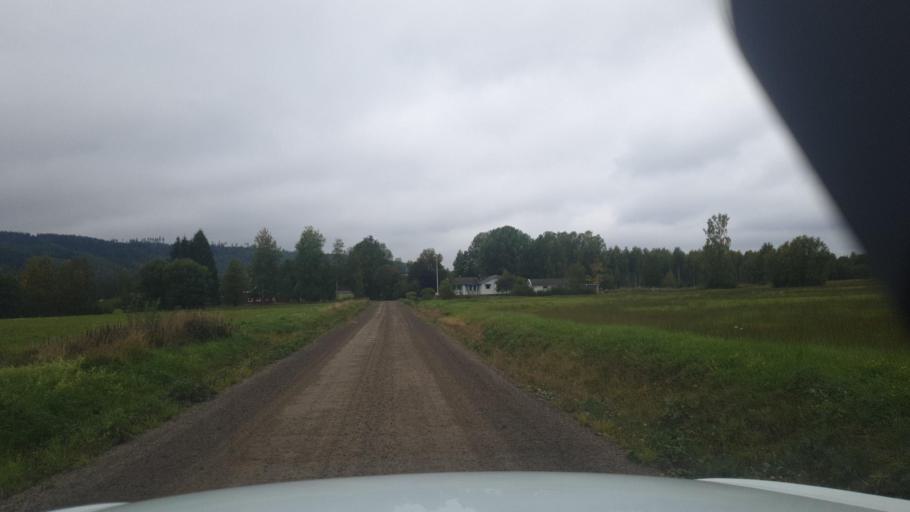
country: SE
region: Vaermland
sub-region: Sunne Kommun
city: Sunne
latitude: 59.8164
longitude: 13.0442
